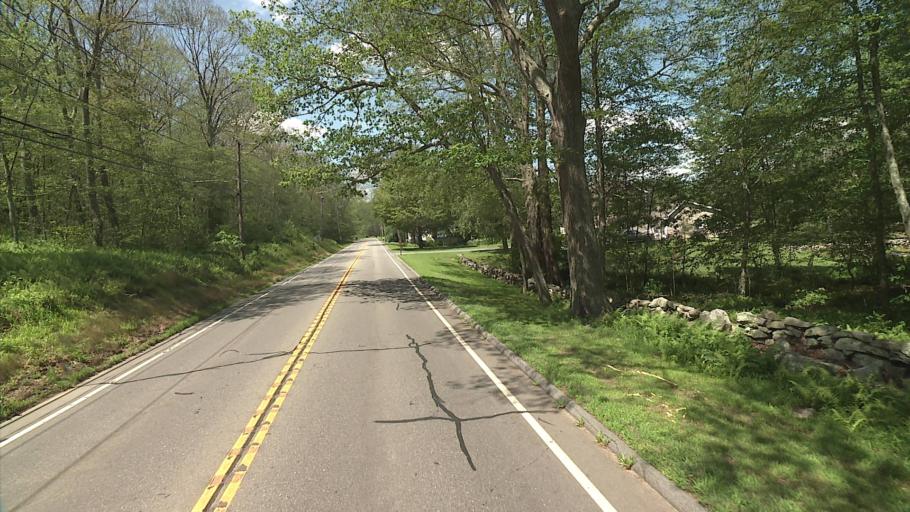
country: US
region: Connecticut
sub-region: New London County
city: Baltic
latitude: 41.7082
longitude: -72.0412
